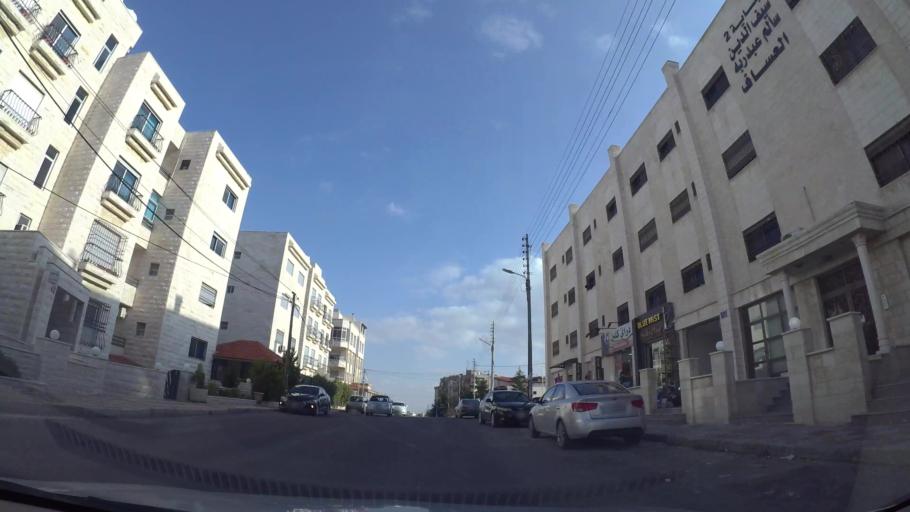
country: JO
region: Amman
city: Al Jubayhah
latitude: 32.0116
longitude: 35.8630
